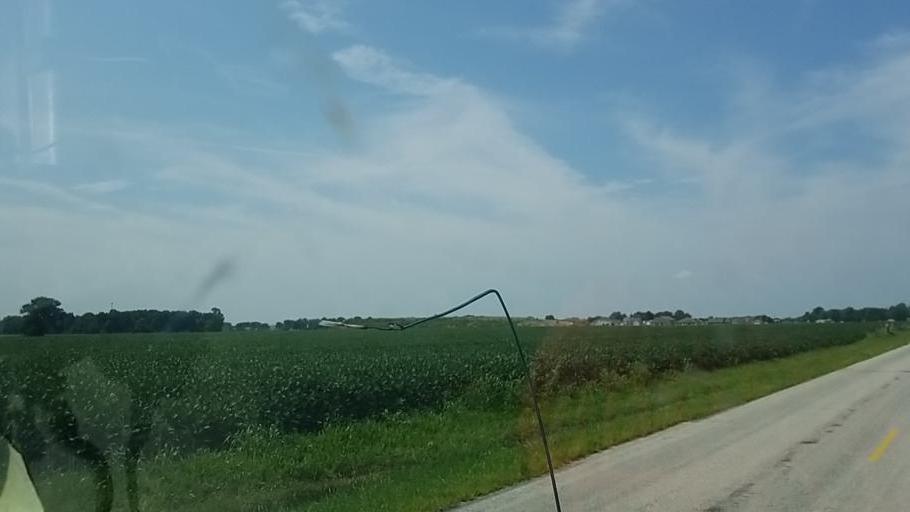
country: US
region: Ohio
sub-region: Marion County
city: Marion
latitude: 40.5978
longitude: -83.0629
